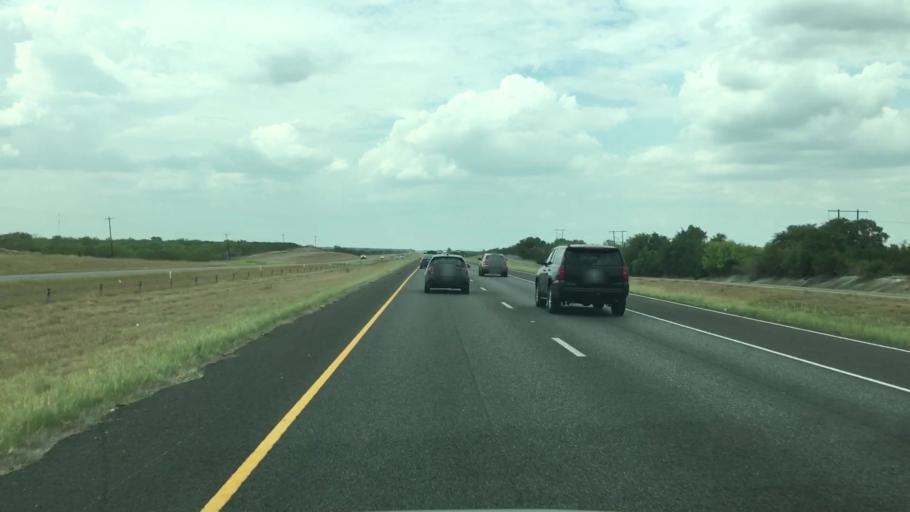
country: US
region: Texas
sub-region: Atascosa County
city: Pleasanton
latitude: 28.8337
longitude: -98.3708
